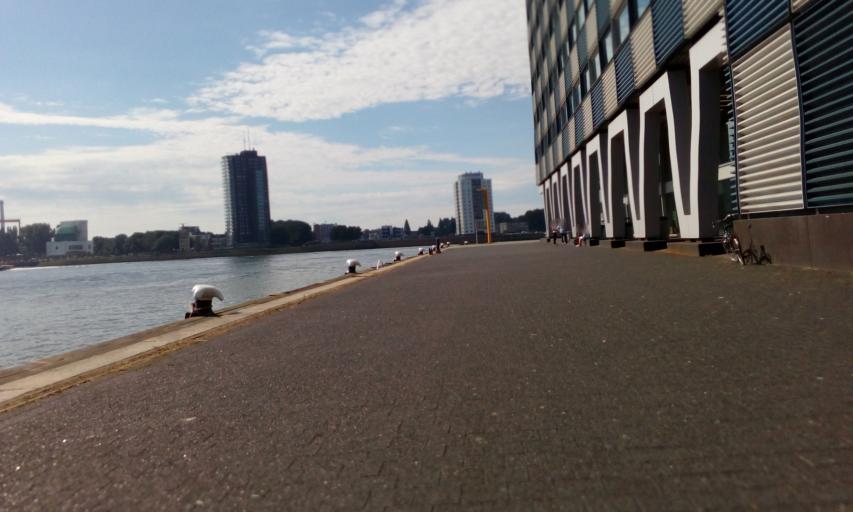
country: NL
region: South Holland
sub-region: Gemeente Rotterdam
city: Delfshaven
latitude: 51.9023
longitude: 4.4616
